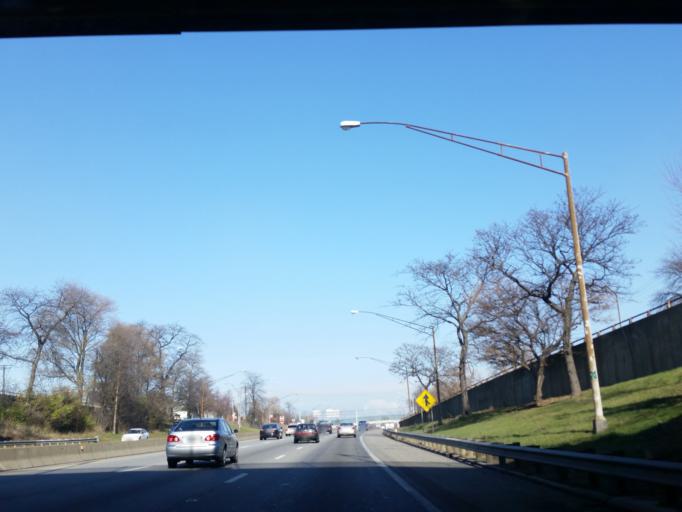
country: US
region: Ohio
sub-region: Cuyahoga County
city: Newburgh Heights
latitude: 41.4558
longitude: -81.6571
